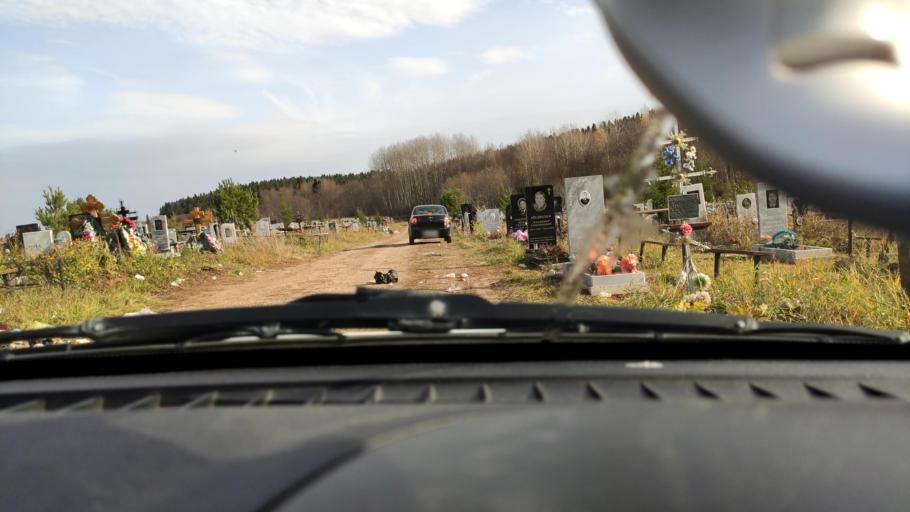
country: RU
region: Perm
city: Kultayevo
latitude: 57.8567
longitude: 55.8707
